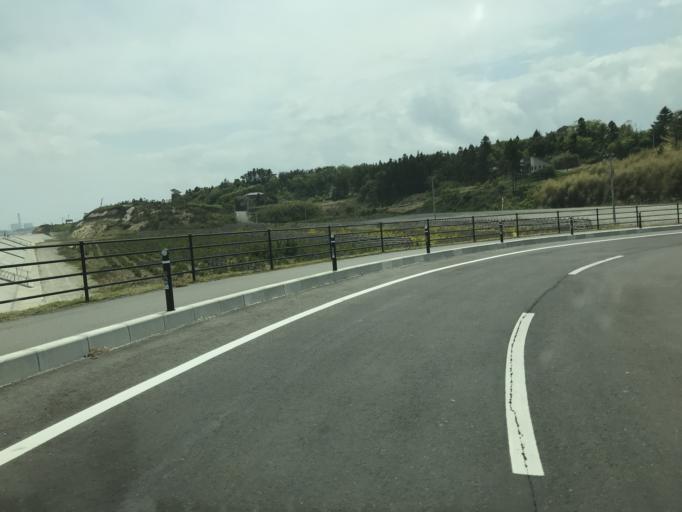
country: JP
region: Miyagi
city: Watari
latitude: 37.8994
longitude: 140.9297
